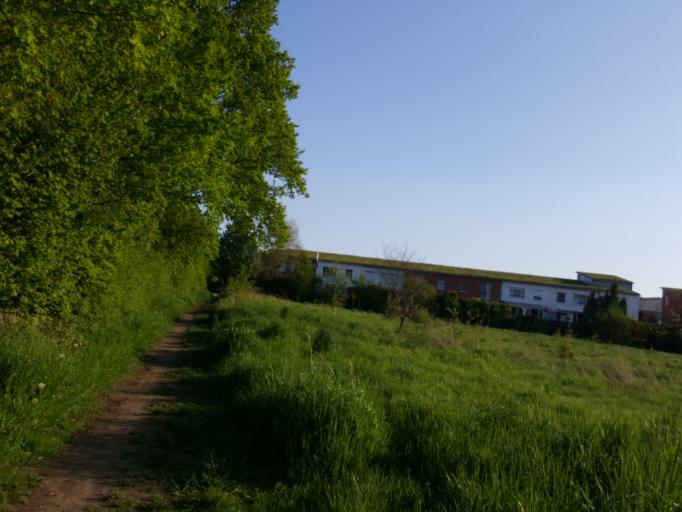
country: DE
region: Schleswig-Holstein
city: Oststeinbek
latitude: 53.5166
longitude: 10.1764
